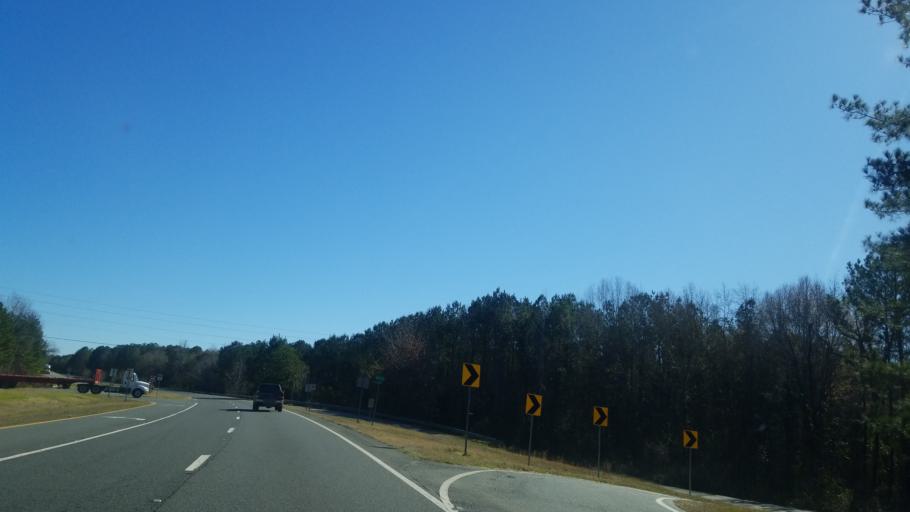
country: US
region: Georgia
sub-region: Talbot County
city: Talbotton
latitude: 32.5466
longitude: -84.7273
